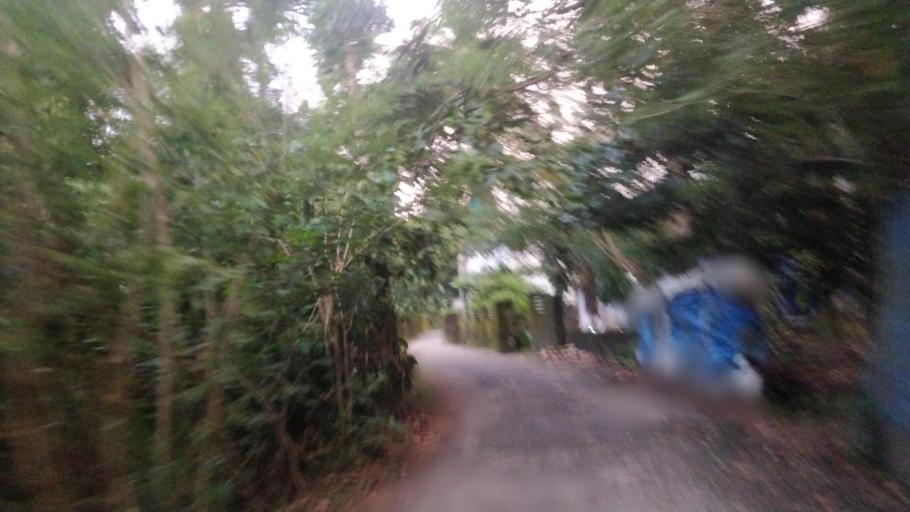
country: IN
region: Kerala
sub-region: Alappuzha
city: Shertallai
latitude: 9.6752
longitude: 76.3356
